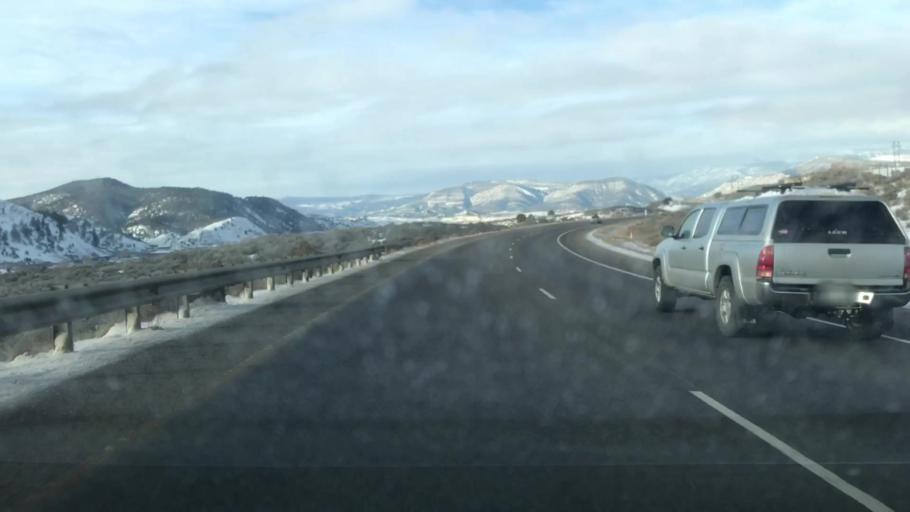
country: US
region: Colorado
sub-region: Eagle County
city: Eagle
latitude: 39.6545
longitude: -106.8527
